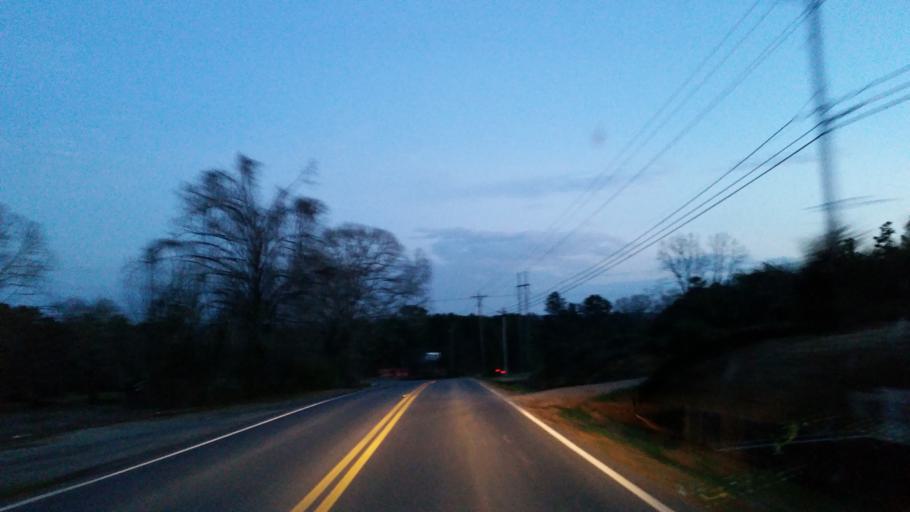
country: US
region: Georgia
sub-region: Cherokee County
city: Ball Ground
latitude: 34.2938
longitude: -84.4387
